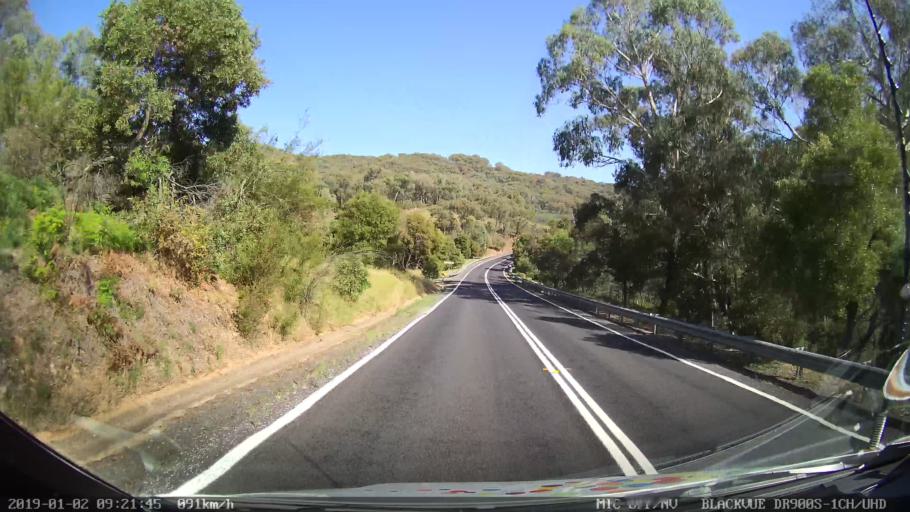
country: AU
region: New South Wales
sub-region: Tumut Shire
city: Tumut
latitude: -35.4022
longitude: 148.2905
